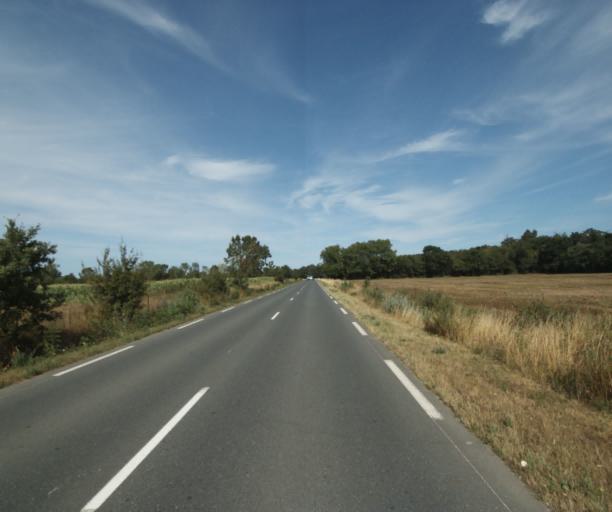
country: FR
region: Midi-Pyrenees
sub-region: Departement du Tarn
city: Soual
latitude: 43.5239
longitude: 2.0874
